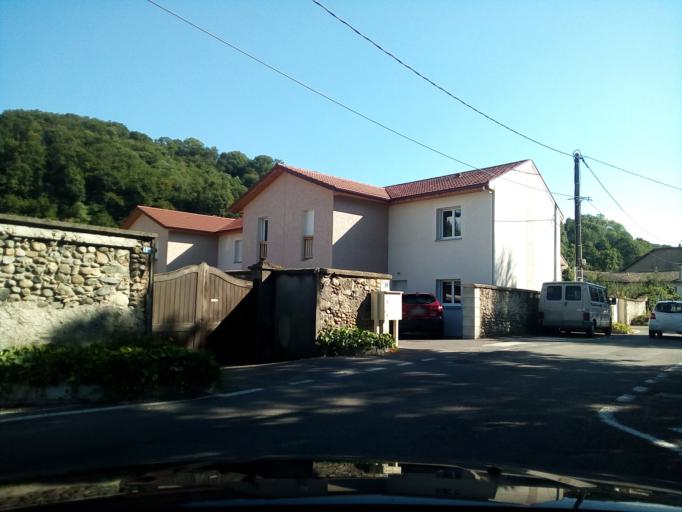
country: FR
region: Rhone-Alpes
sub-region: Departement de l'Isere
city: Echirolles
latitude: 45.1395
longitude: 5.7188
